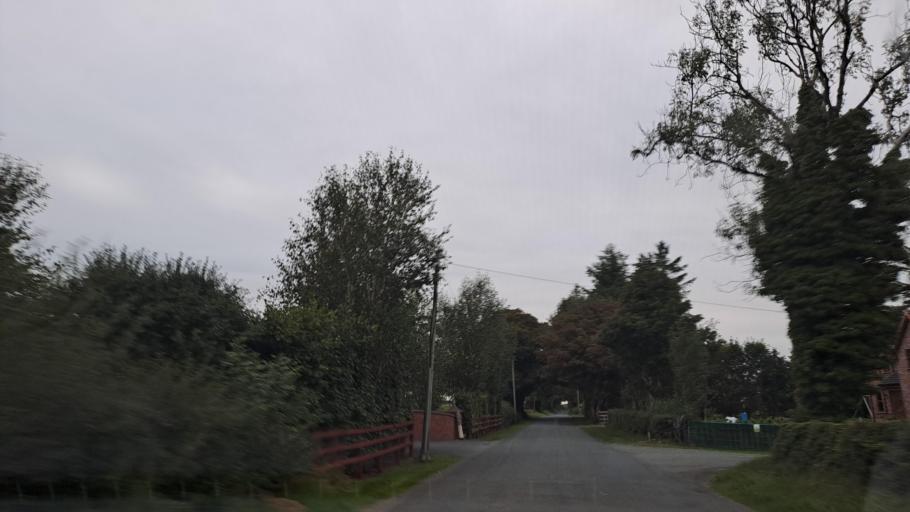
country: IE
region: Ulster
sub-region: County Monaghan
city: Carrickmacross
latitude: 54.0247
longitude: -6.7897
